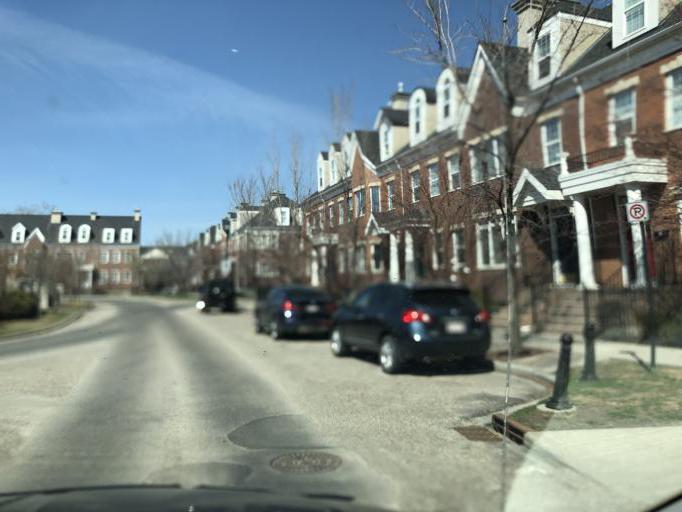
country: CA
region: Alberta
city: Calgary
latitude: 51.0210
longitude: -114.1137
